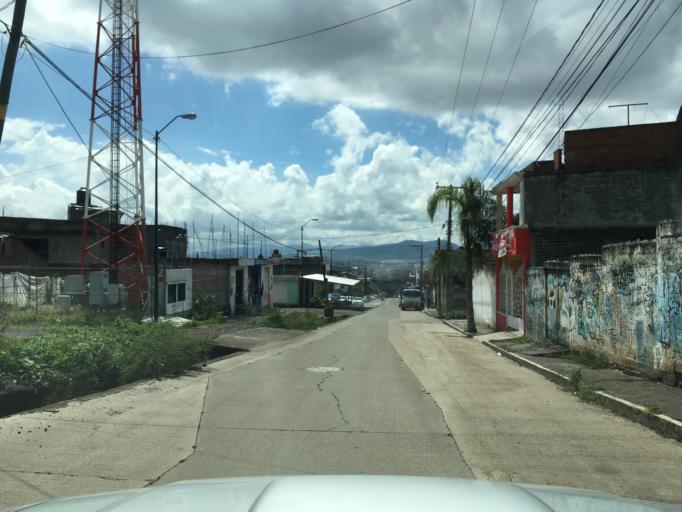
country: MX
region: Michoacan
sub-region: Tarimbaro
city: Fraccionamiento Metropolis II
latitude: 19.7264
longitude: -101.2321
